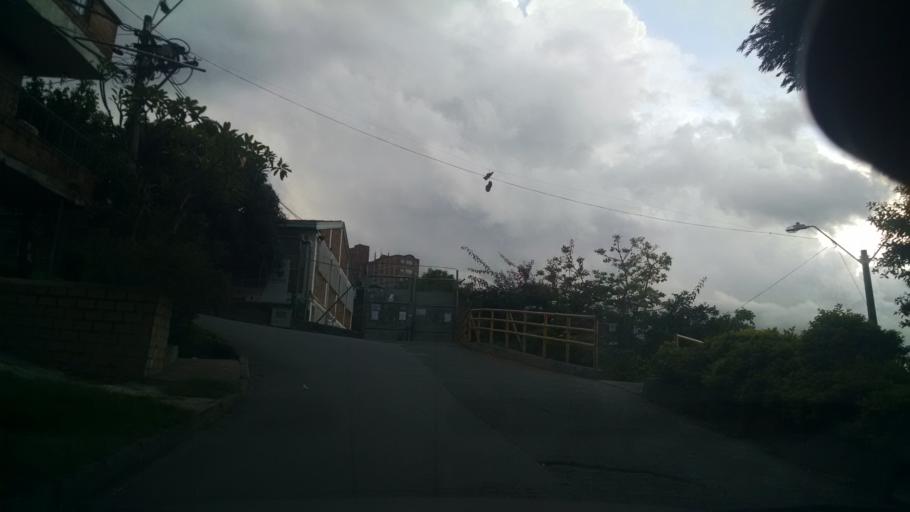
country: CO
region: Antioquia
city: Medellin
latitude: 6.2626
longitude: -75.6110
